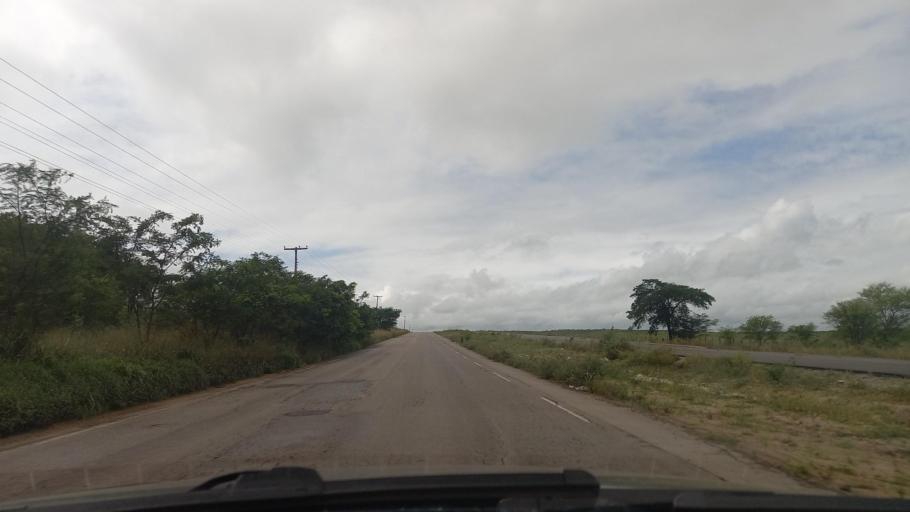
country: BR
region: Alagoas
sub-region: Batalha
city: Batalha
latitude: -9.6525
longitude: -37.1814
